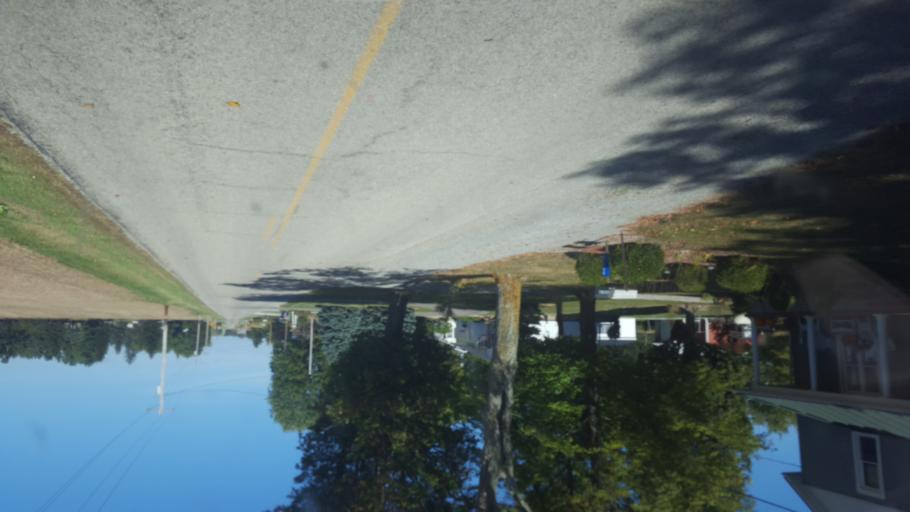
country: US
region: Ohio
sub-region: Huron County
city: Willard
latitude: 40.9682
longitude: -82.7910
